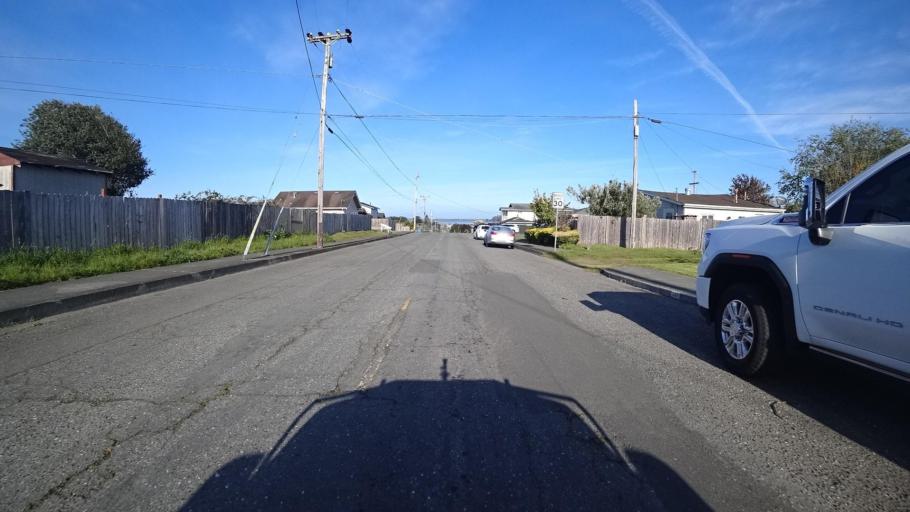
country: US
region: California
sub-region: Humboldt County
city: Bayview
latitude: 40.7741
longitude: -124.1805
